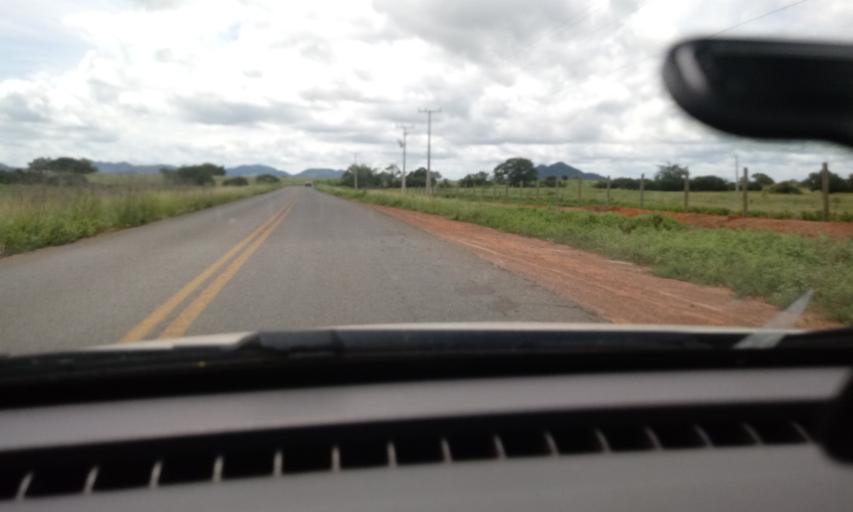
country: BR
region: Bahia
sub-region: Guanambi
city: Guanambi
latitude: -14.1049
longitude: -42.8685
